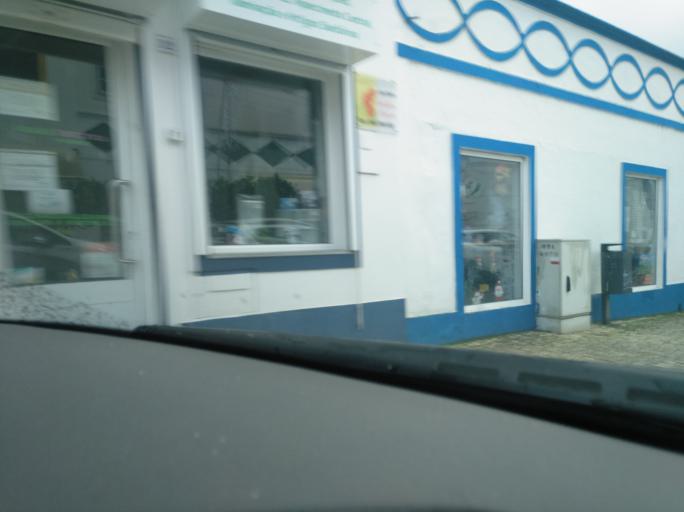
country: PT
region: Beja
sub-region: Mertola
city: Mertola
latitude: 37.6407
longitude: -7.6593
